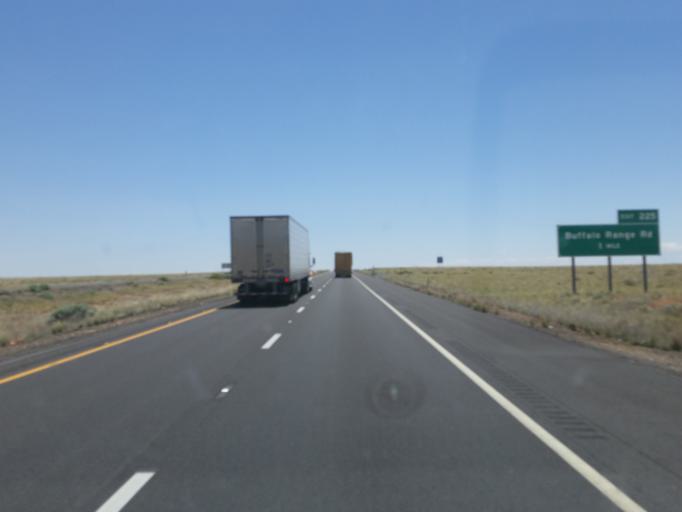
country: US
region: Arizona
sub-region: Coconino County
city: Flagstaff
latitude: 35.1359
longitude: -111.2029
